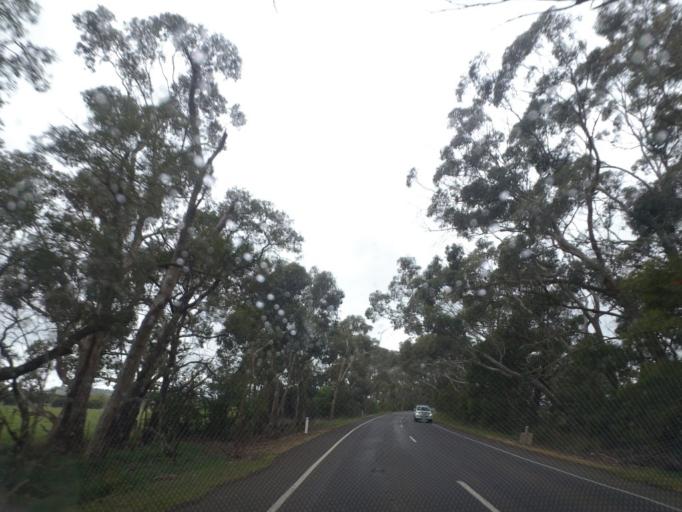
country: AU
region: Victoria
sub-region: Hume
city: Sunbury
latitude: -37.3442
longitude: 144.6909
